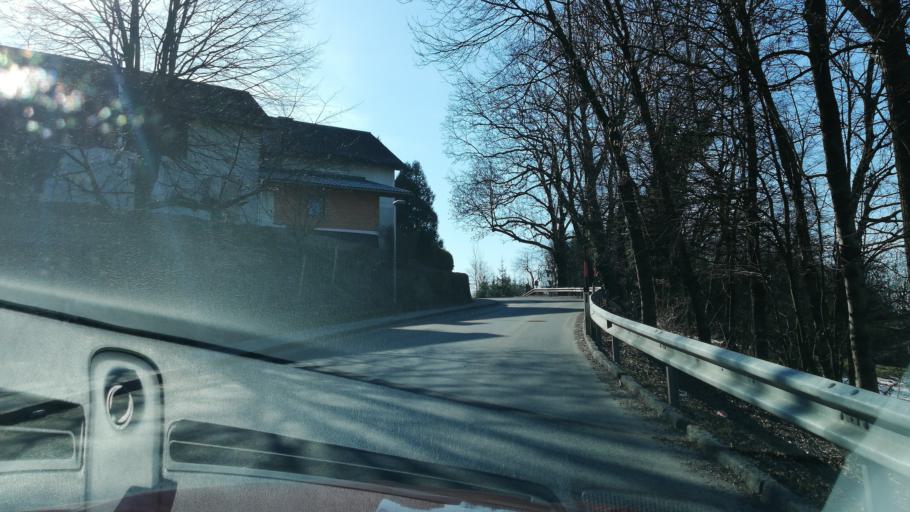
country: AT
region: Upper Austria
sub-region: Politischer Bezirk Vocklabruck
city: Lenzing
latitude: 47.9737
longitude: 13.6239
